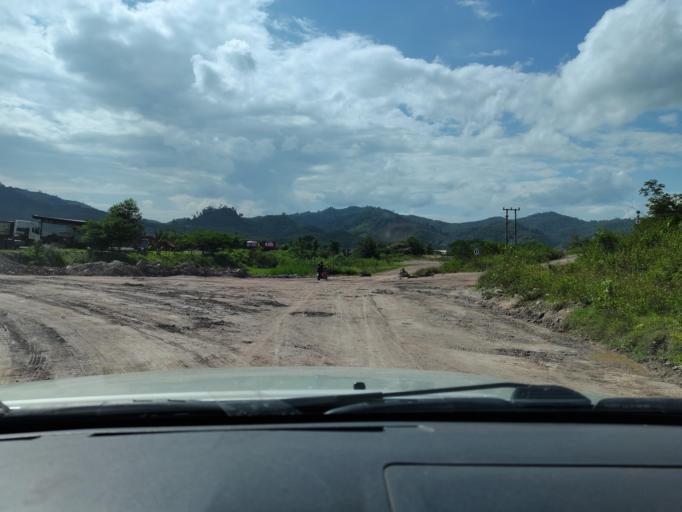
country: LA
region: Loungnamtha
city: Muang Nale
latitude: 20.5891
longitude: 101.0588
